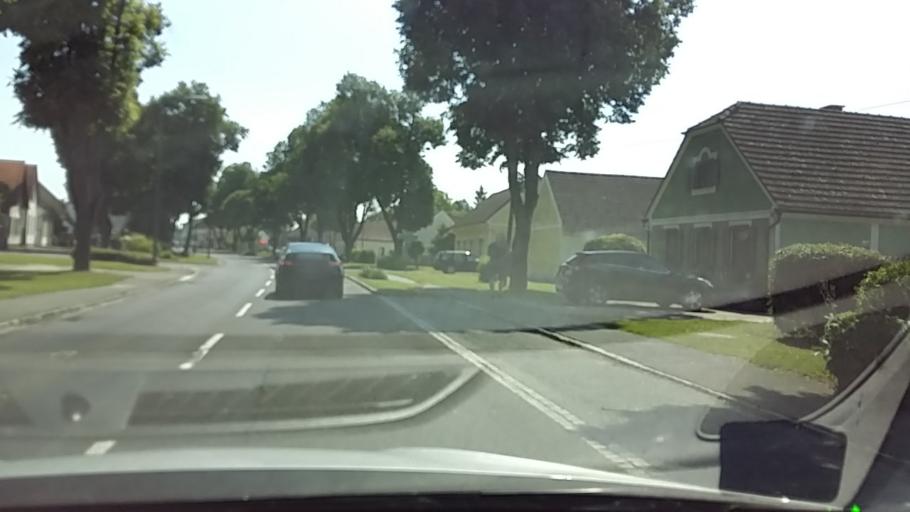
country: AT
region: Burgenland
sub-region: Politischer Bezirk Jennersdorf
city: Mogersdorf
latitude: 46.9474
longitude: 16.2272
